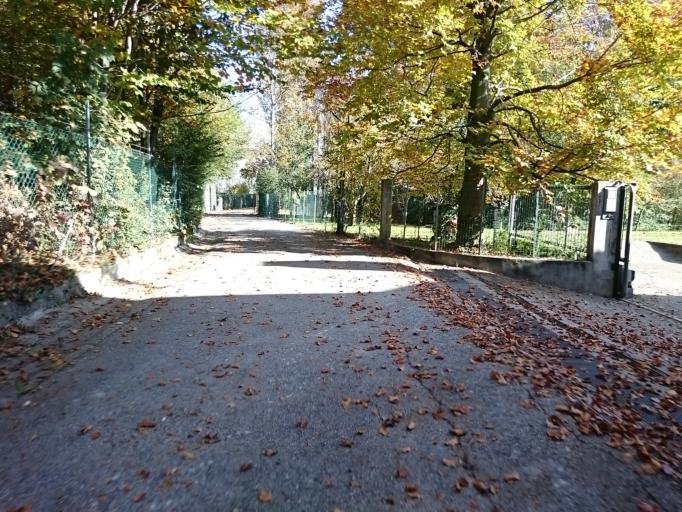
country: IT
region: Veneto
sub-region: Provincia di Padova
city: Piazzola sul Brenta
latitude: 45.5467
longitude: 11.7760
